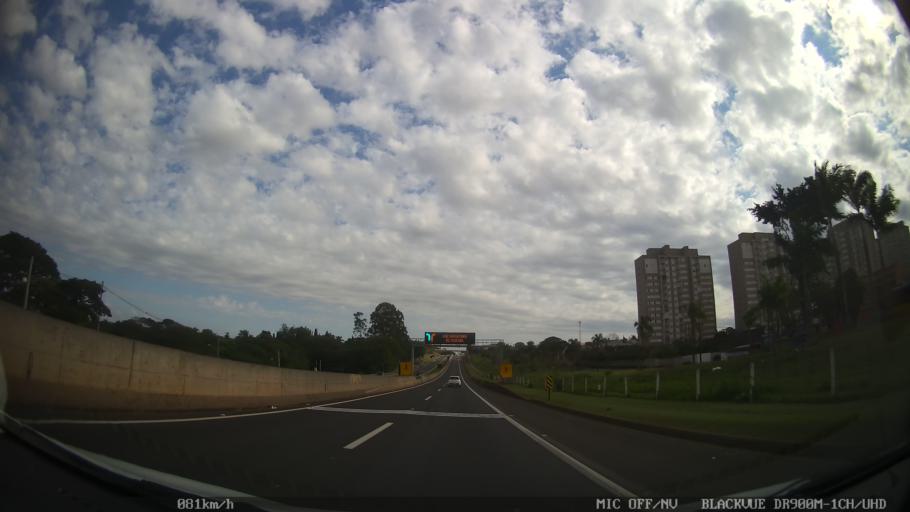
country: BR
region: Sao Paulo
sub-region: Limeira
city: Limeira
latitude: -22.5657
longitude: -47.4331
